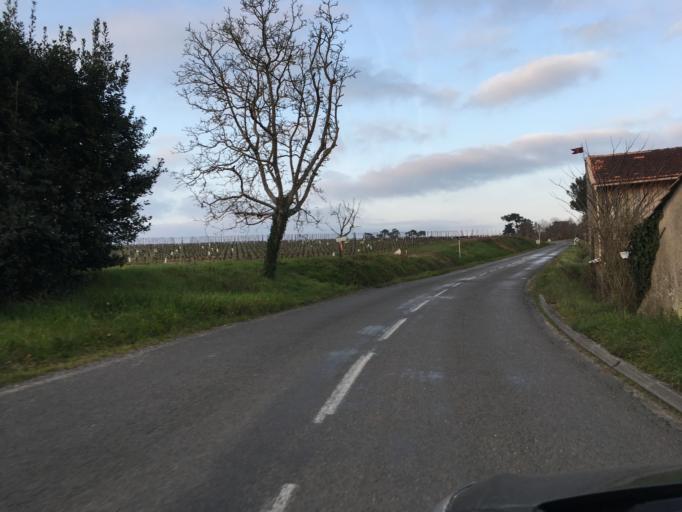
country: FR
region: Aquitaine
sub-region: Departement de la Gironde
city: Saint-Ciers-sur-Gironde
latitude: 45.3139
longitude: -0.5961
